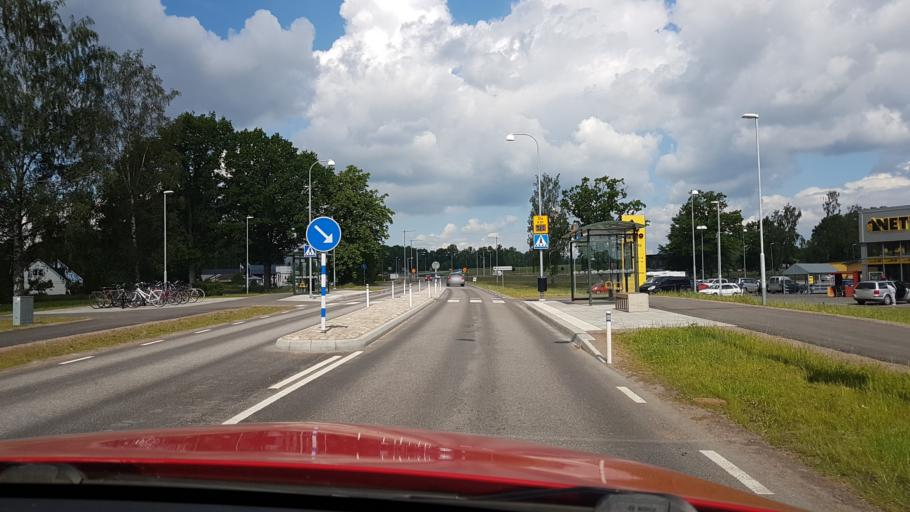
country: SE
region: Vaestra Goetaland
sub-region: Hjo Kommun
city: Hjo
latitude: 58.3119
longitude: 14.2800
